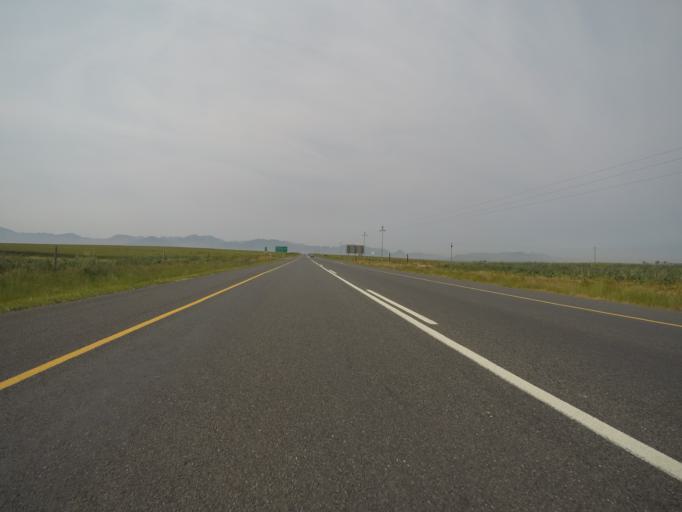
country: ZA
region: Western Cape
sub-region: Cape Winelands District Municipality
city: Noorder-Paarl
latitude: -33.5669
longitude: 18.8869
